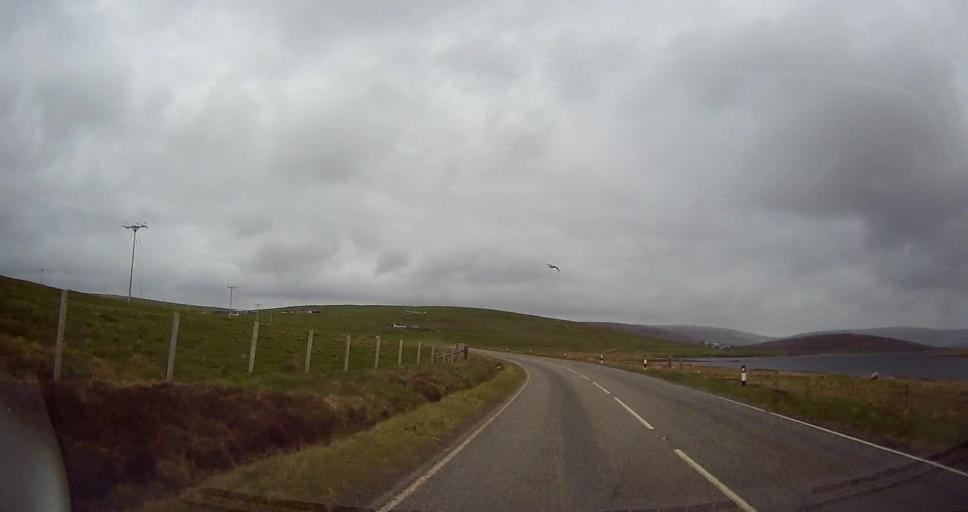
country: GB
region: Scotland
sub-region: Shetland Islands
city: Lerwick
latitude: 60.2564
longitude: -1.4279
